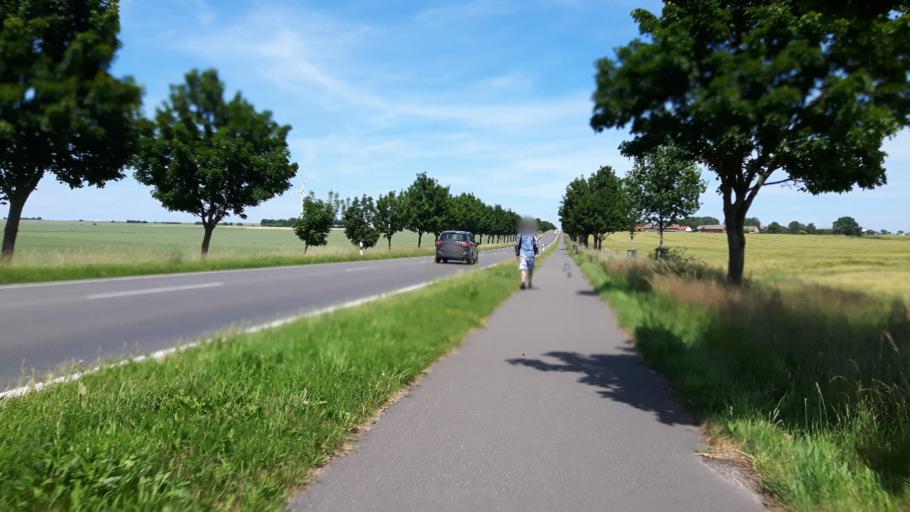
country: DE
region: Saxony-Anhalt
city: Kropstadt
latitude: 52.0061
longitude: 12.7832
